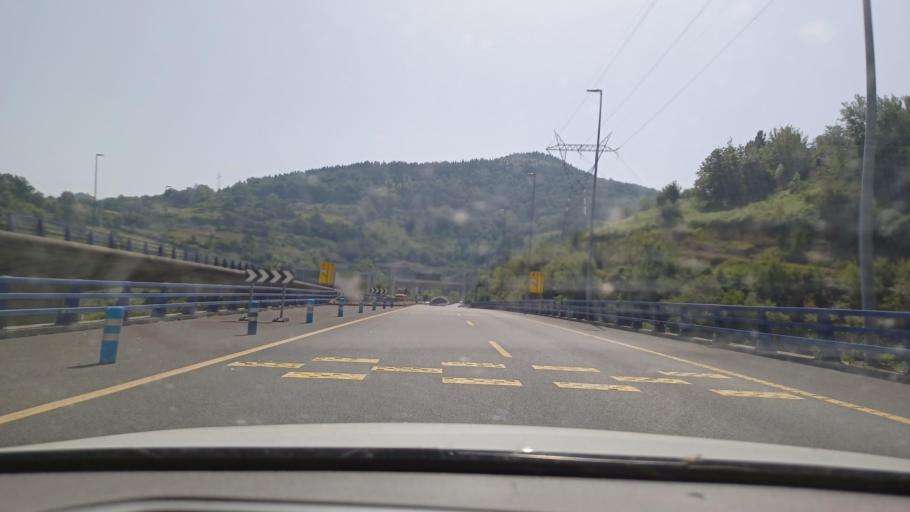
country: ES
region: Basque Country
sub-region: Bizkaia
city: Bilbao
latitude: 43.2378
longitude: -2.9502
